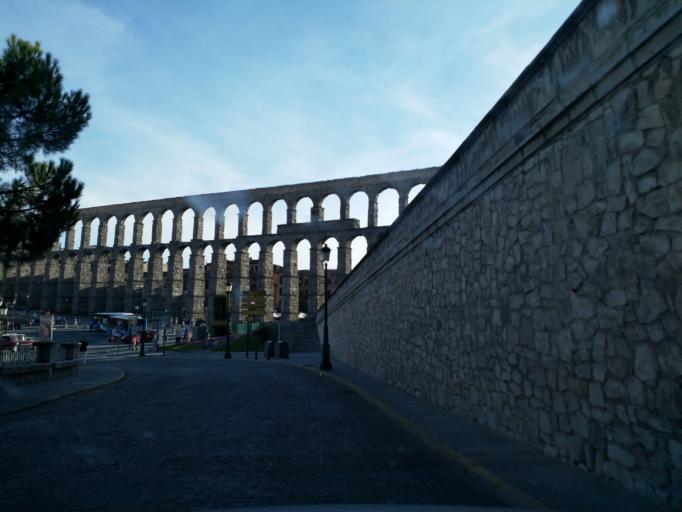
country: ES
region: Castille and Leon
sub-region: Provincia de Segovia
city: Segovia
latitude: 40.9489
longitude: -4.1174
